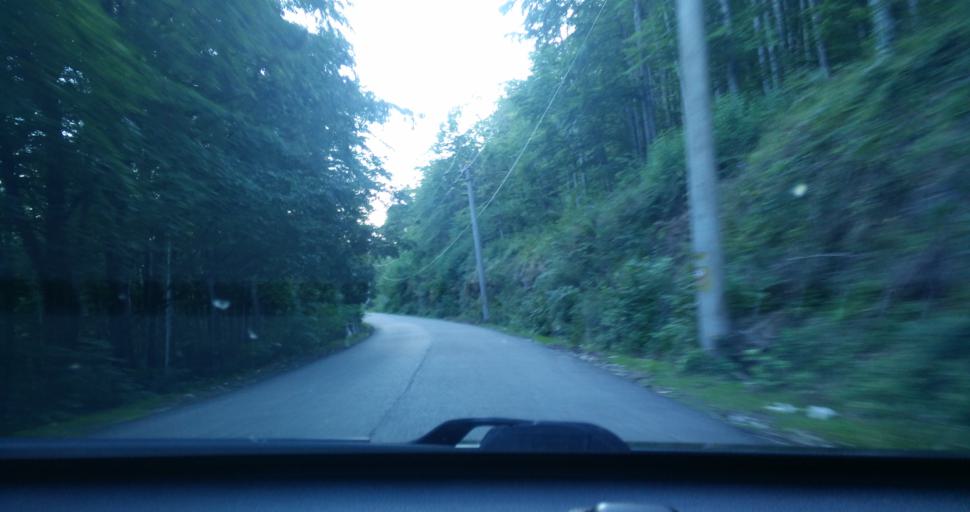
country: RO
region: Bihor
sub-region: Oras Nucet
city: Nucet
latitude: 46.5104
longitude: 22.6222
